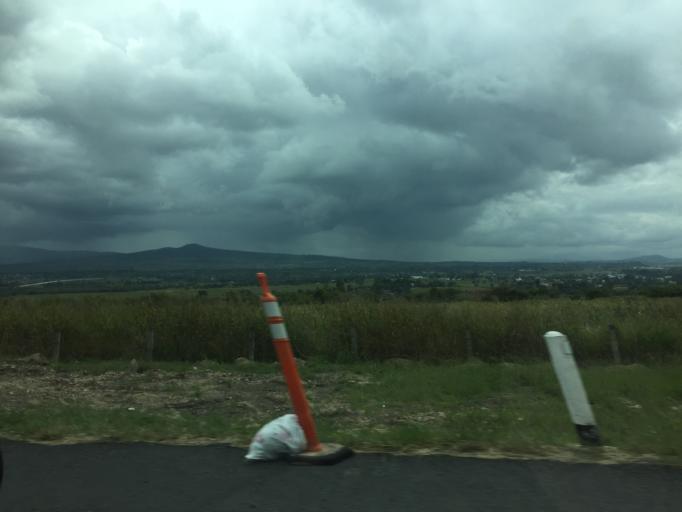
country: MX
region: Jalisco
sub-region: Zapotlanejo
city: La Mezquitera
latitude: 20.5896
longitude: -103.1033
